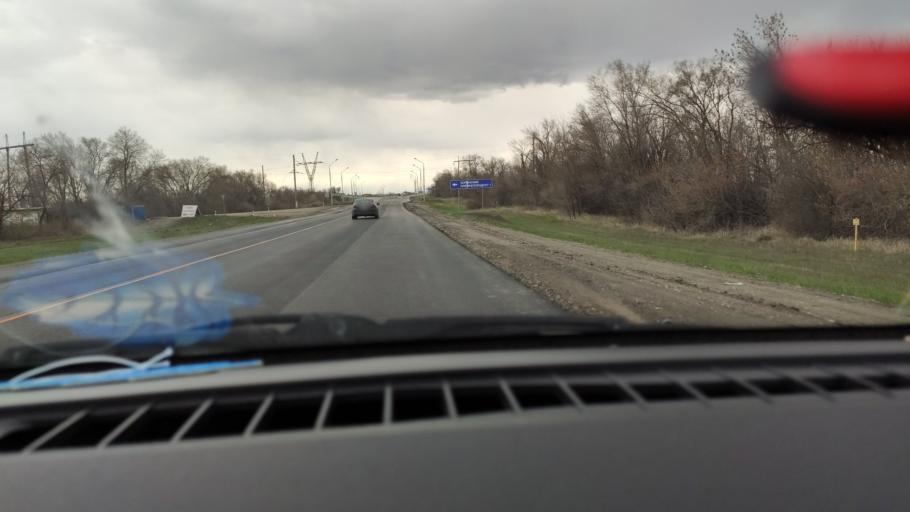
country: RU
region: Saratov
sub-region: Saratovskiy Rayon
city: Saratov
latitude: 51.6722
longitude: 46.0002
